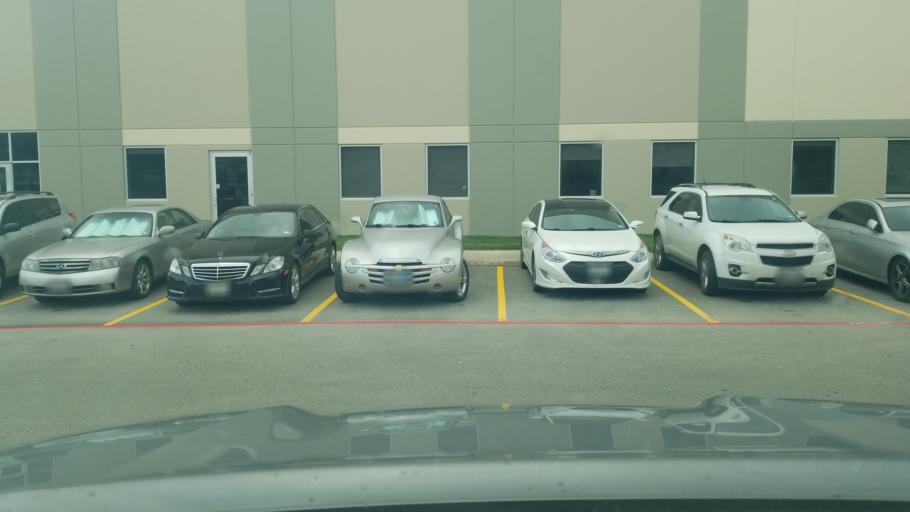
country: US
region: Texas
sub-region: Bexar County
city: Live Oak
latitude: 29.6001
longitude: -98.3652
